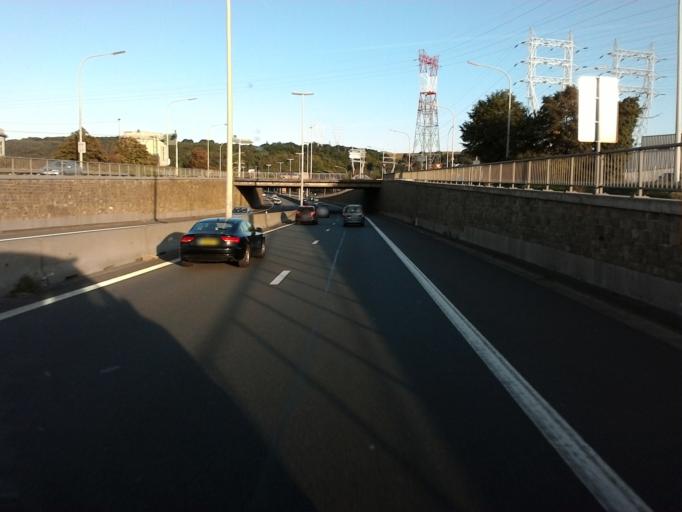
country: BE
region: Wallonia
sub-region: Province de Liege
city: Herstal
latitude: 50.6506
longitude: 5.6290
